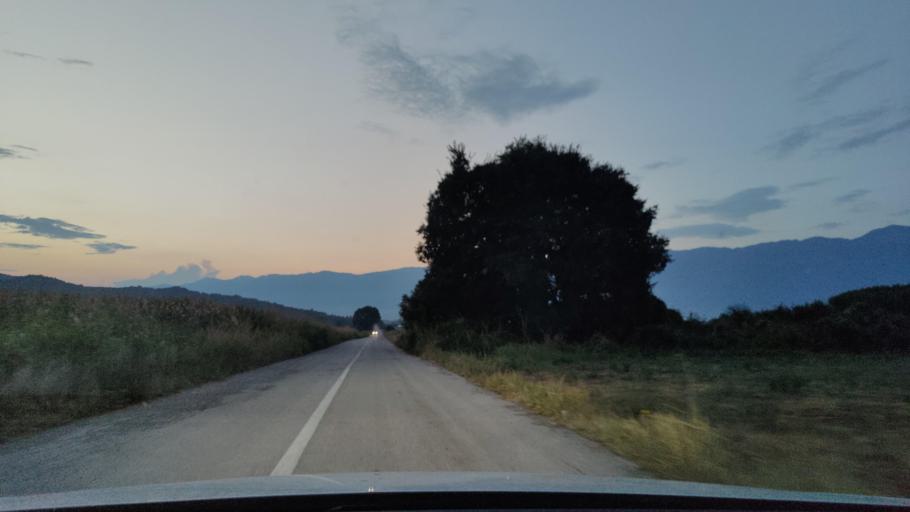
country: GR
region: Central Macedonia
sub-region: Nomos Serron
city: Chrysochorafa
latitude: 41.1849
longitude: 23.1034
